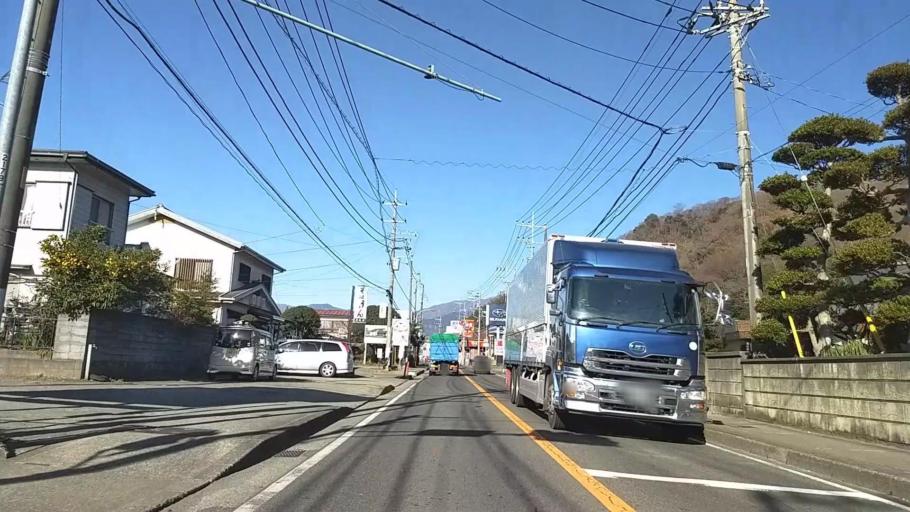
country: JP
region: Kanagawa
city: Hadano
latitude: 35.3664
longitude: 139.2421
